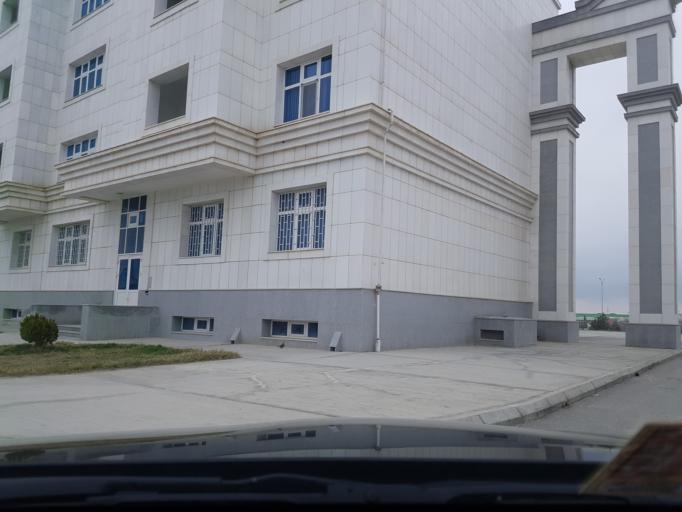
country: TM
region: Ahal
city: Abadan
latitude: 38.1652
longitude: 57.9319
